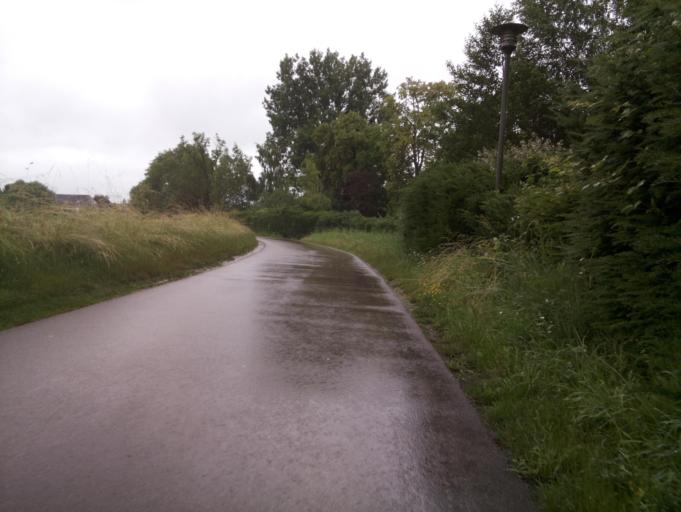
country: FR
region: Picardie
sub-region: Departement de la Somme
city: Dreuil-les-Amiens
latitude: 49.9181
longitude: 2.2256
